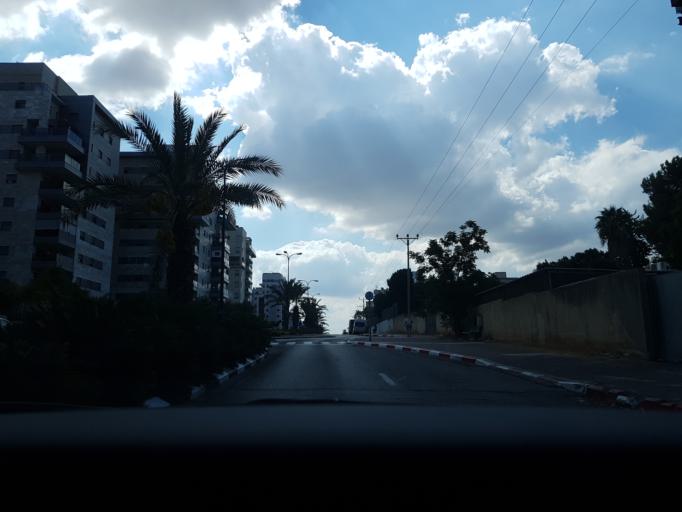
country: IL
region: Central District
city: Ness Ziona
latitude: 31.9037
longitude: 34.8187
